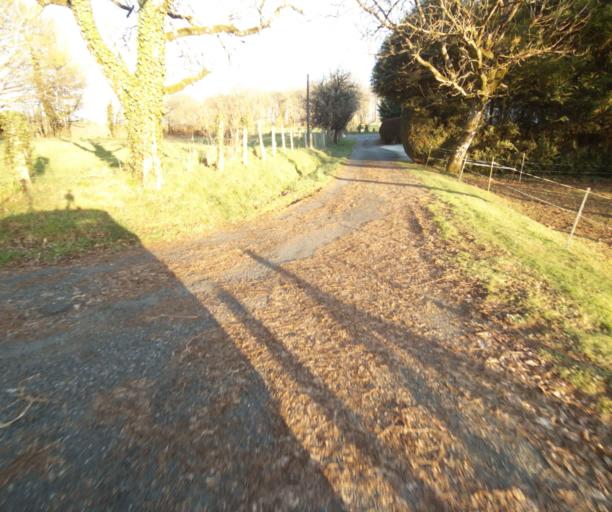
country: FR
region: Limousin
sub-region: Departement de la Correze
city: Saint-Clement
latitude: 45.3498
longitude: 1.7004
